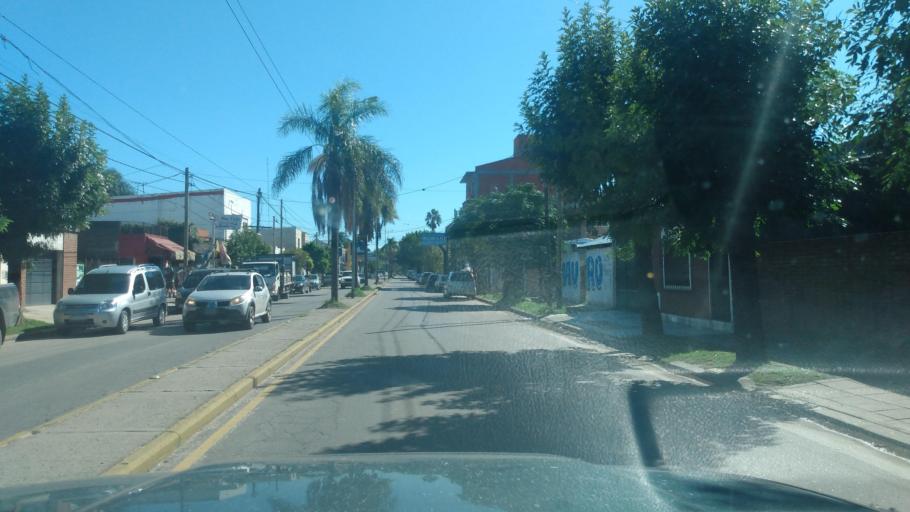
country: AR
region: Buenos Aires
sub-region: Partido de General Rodriguez
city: General Rodriguez
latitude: -34.6006
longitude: -58.9485
